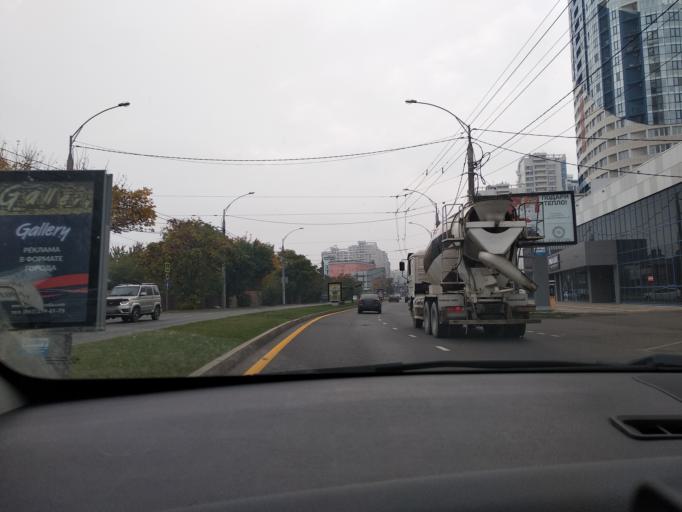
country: RU
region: Krasnodarskiy
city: Krasnodar
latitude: 45.0275
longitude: 38.9597
